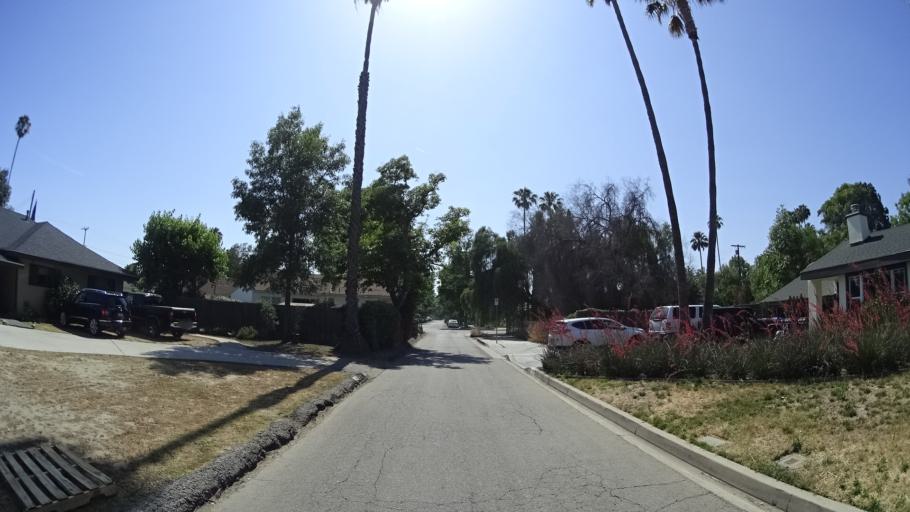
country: US
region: California
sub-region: Los Angeles County
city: Sherman Oaks
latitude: 34.1658
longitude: -118.4524
